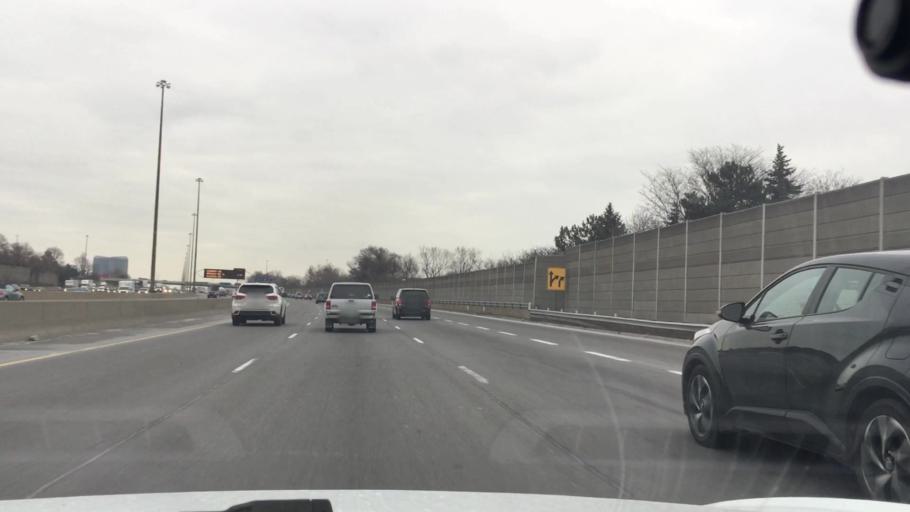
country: CA
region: Ontario
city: Scarborough
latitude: 43.7677
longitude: -79.3138
